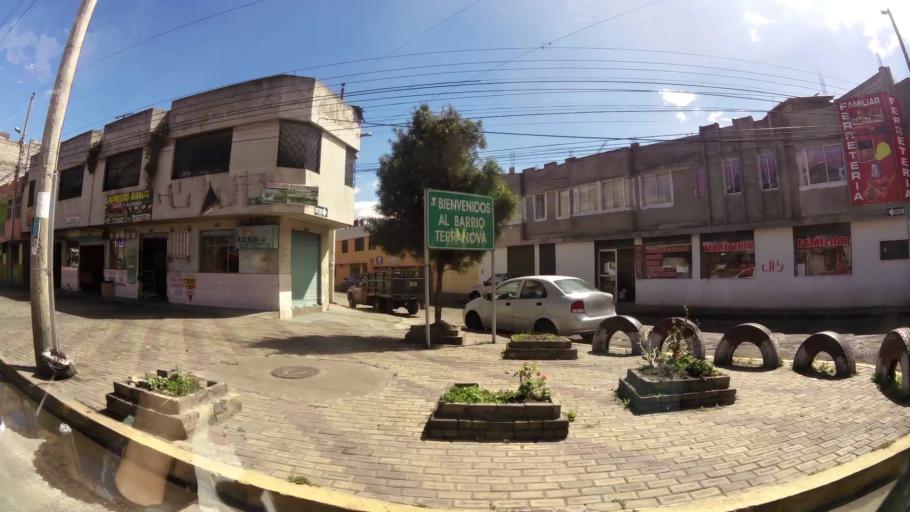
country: EC
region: Pichincha
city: Quito
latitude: -0.3028
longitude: -78.5519
